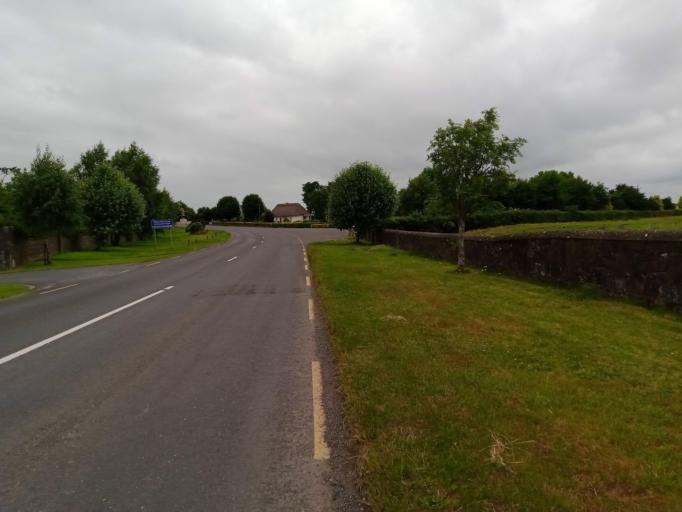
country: IE
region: Leinster
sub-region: Kilkenny
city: Callan
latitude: 52.5513
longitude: -7.3969
